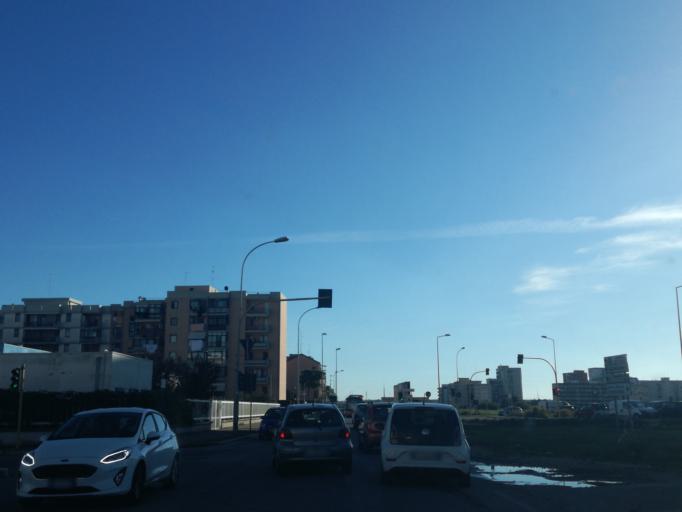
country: IT
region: Apulia
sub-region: Provincia di Bari
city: San Paolo
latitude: 41.1215
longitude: 16.7864
